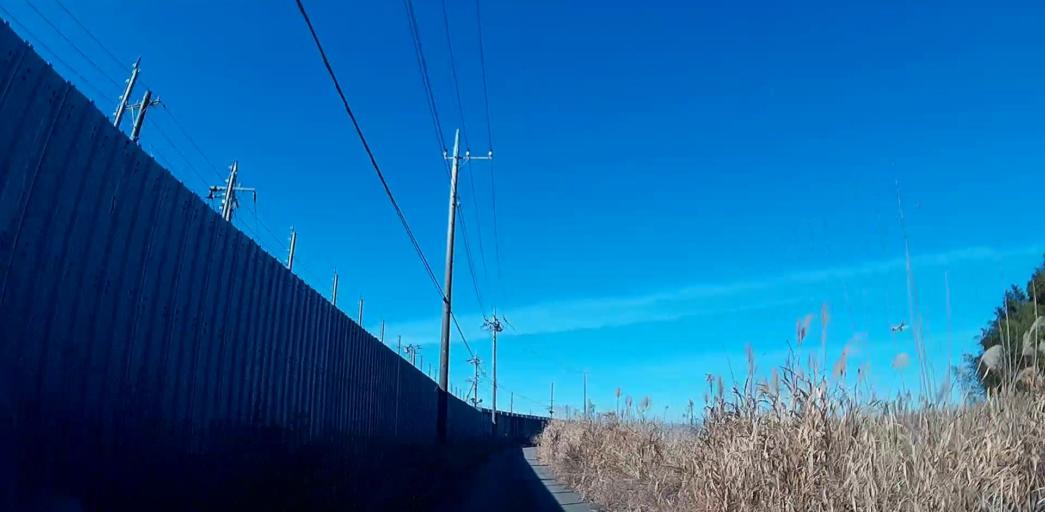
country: JP
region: Chiba
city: Narita
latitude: 35.7679
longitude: 140.4016
